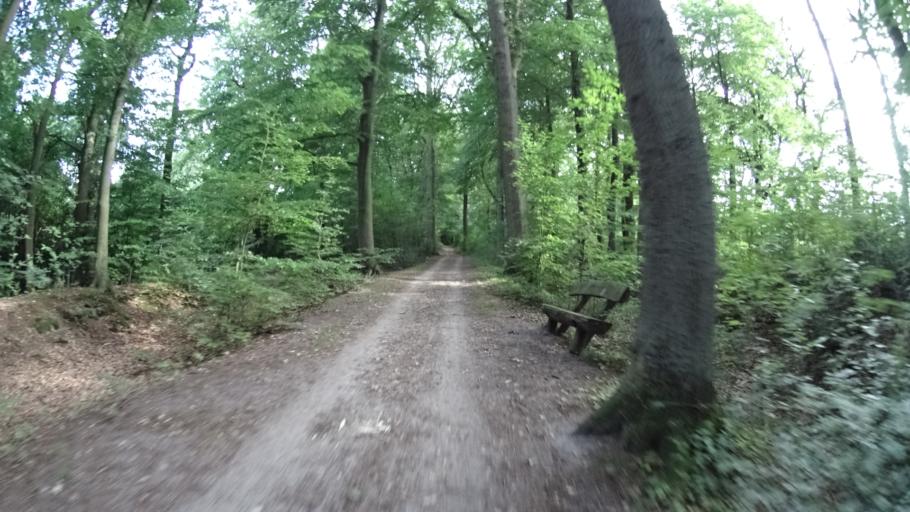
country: DE
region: Lower Saxony
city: Vogelsen
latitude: 53.2706
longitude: 10.3580
